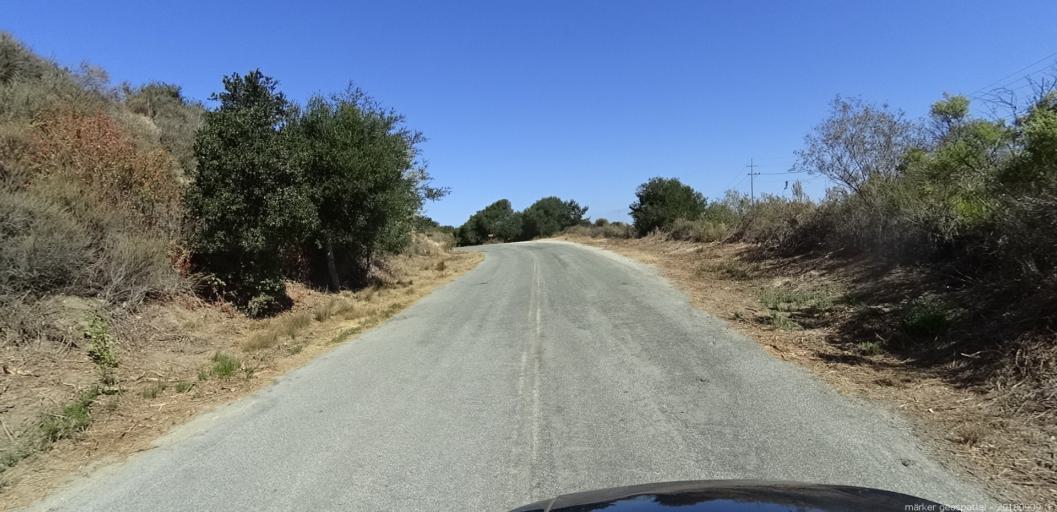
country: US
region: California
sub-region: Monterey County
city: Salinas
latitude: 36.6254
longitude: -121.6888
